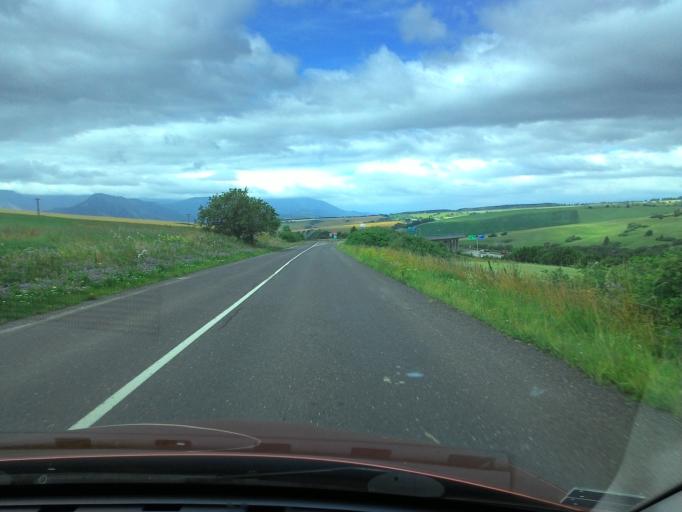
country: SK
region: Zilinsky
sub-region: Okres Liptovsky Mikulas
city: Hybe
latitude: 49.0570
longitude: 19.8638
